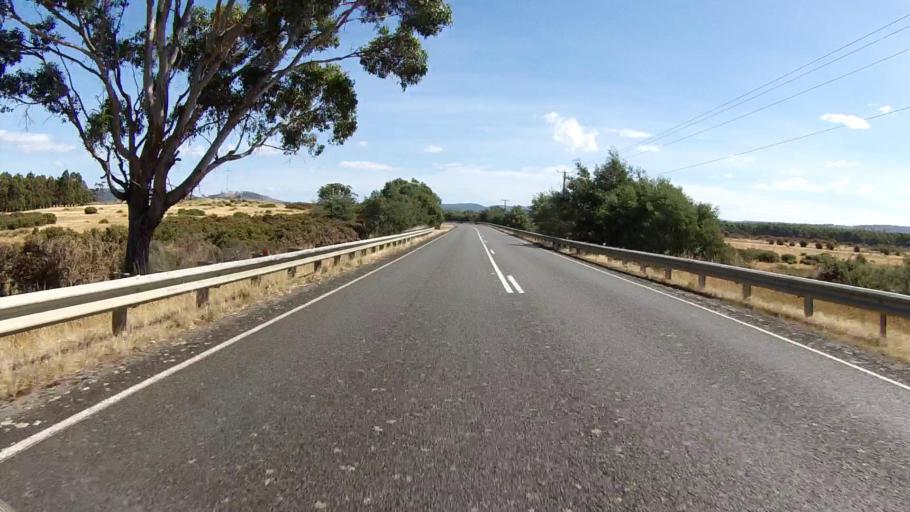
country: AU
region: Tasmania
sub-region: Sorell
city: Sorell
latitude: -42.5935
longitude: 147.7917
